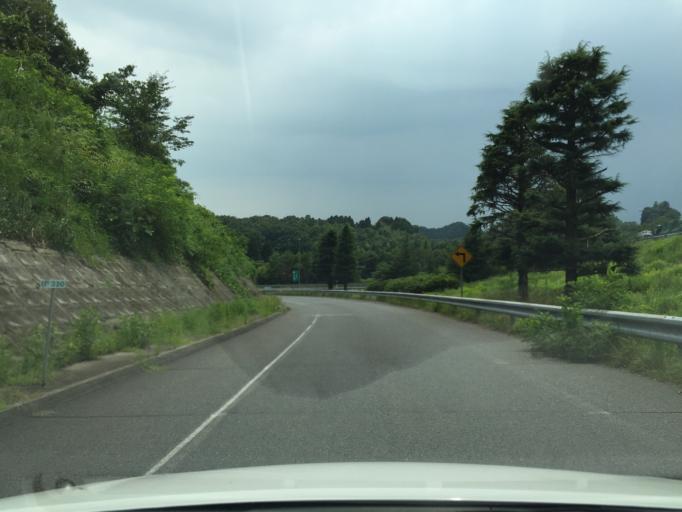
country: JP
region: Fukushima
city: Iwaki
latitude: 37.0036
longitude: 140.8107
